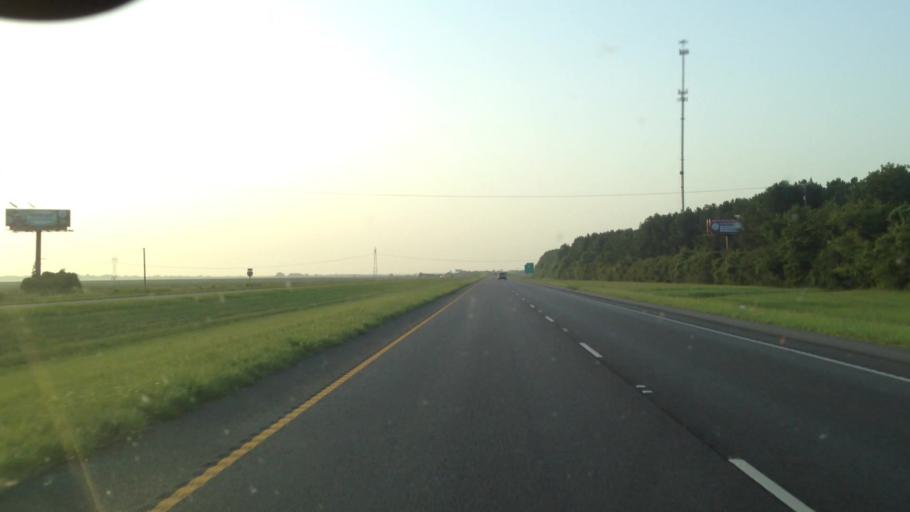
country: US
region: Louisiana
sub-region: Natchitoches Parish
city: Campti
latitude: 31.8437
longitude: -93.2887
